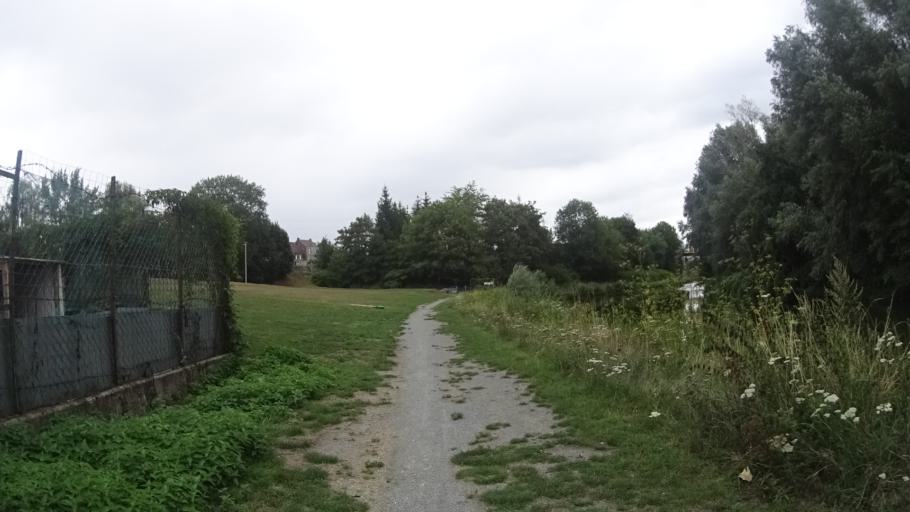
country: FR
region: Nord-Pas-de-Calais
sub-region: Departement du Nord
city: Hautmont
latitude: 50.2603
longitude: 3.9218
